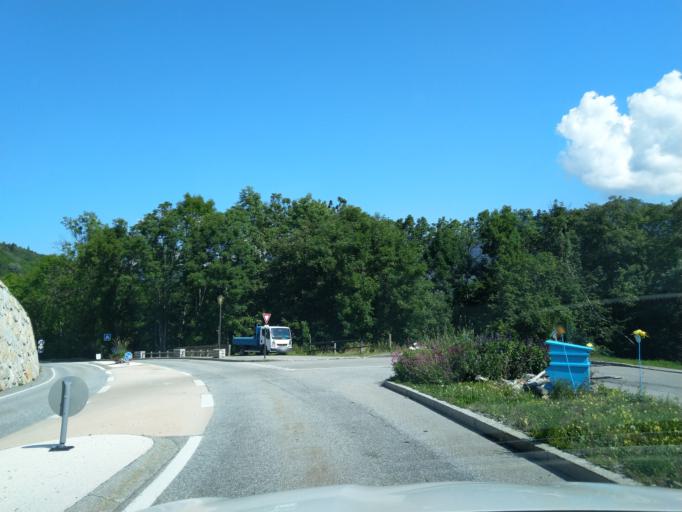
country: FR
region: Rhone-Alpes
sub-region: Departement de la Savoie
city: Les Allues
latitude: 45.4350
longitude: 6.5559
